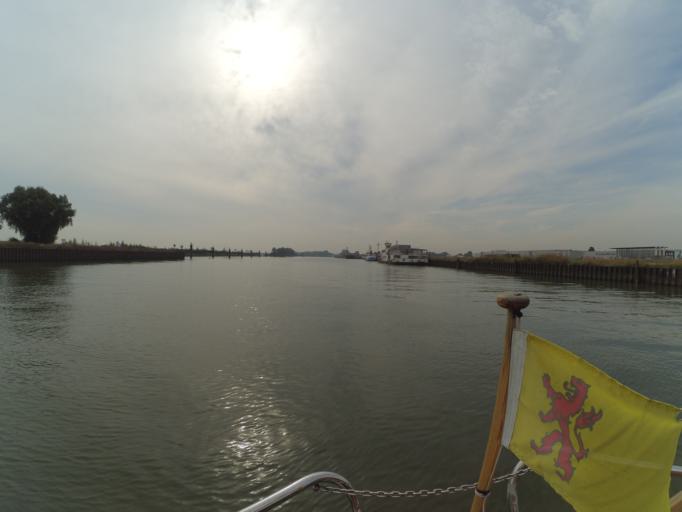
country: NL
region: South Holland
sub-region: Gemeente Alblasserdam
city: Alblasserdam
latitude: 51.8470
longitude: 4.6591
